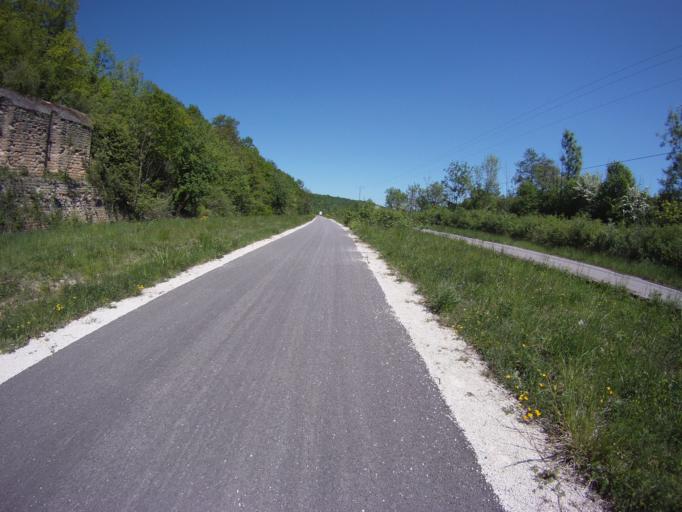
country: FR
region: Lorraine
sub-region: Departement de Meurthe-et-Moselle
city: Villey-Saint-Etienne
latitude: 48.7457
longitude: 6.0043
